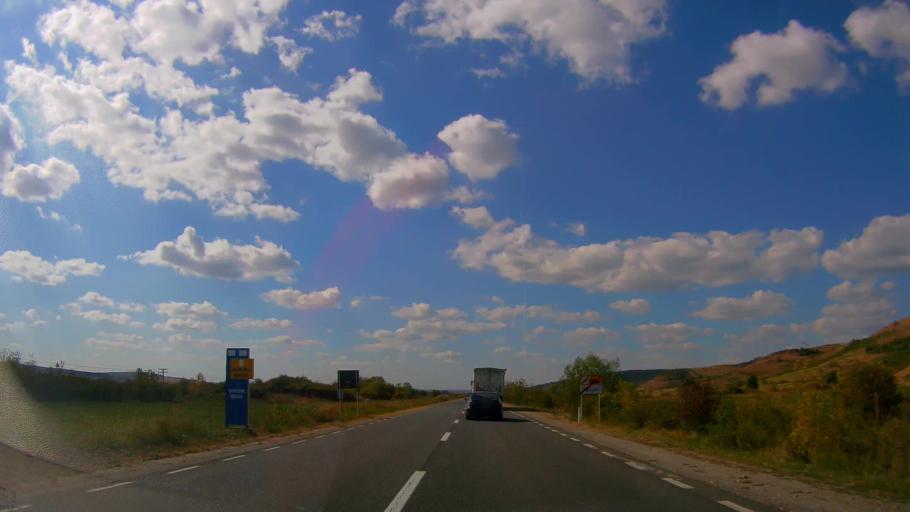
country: RO
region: Salaj
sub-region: Comuna Bocsa
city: Bocsa
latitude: 47.3201
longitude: 22.8961
